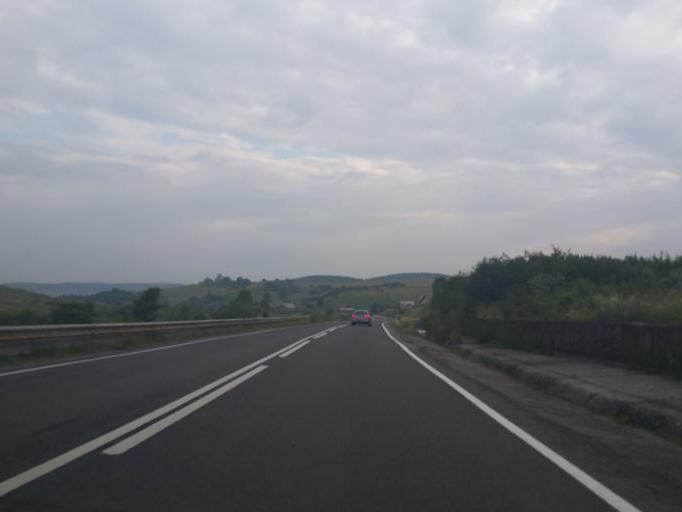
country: RO
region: Cluj
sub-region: Comuna Sanpaul
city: Sanpaul
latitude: 46.9166
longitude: 23.4225
